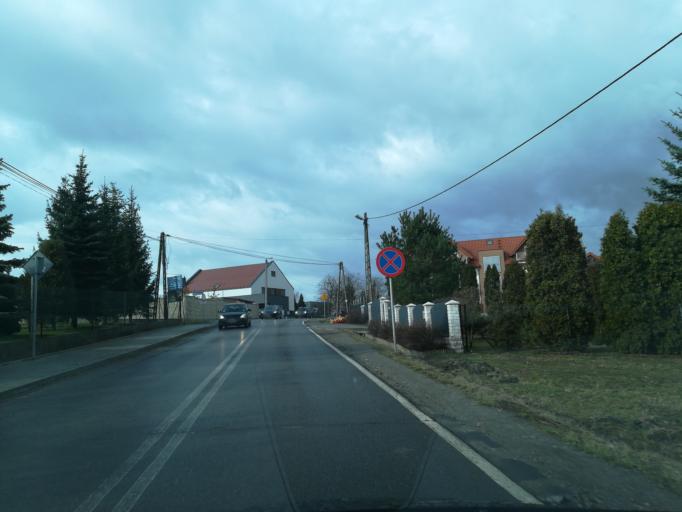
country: PL
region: Lesser Poland Voivodeship
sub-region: Powiat krakowski
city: Libertow
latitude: 49.9847
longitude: 19.8980
